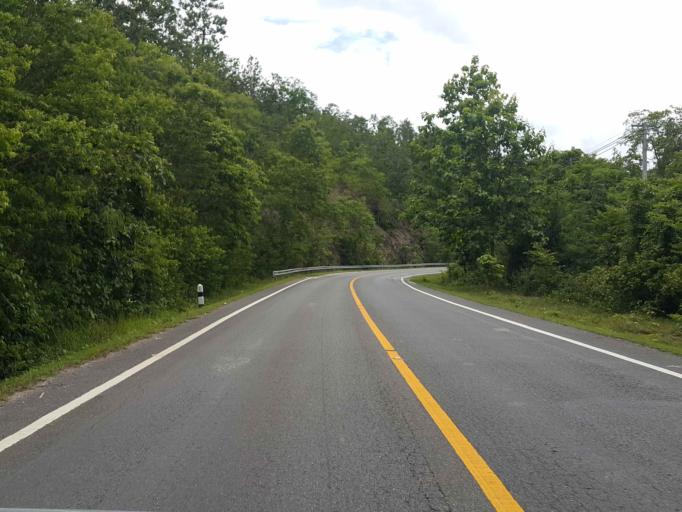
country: TH
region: Chiang Mai
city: Chom Thong
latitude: 18.5159
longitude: 98.6575
